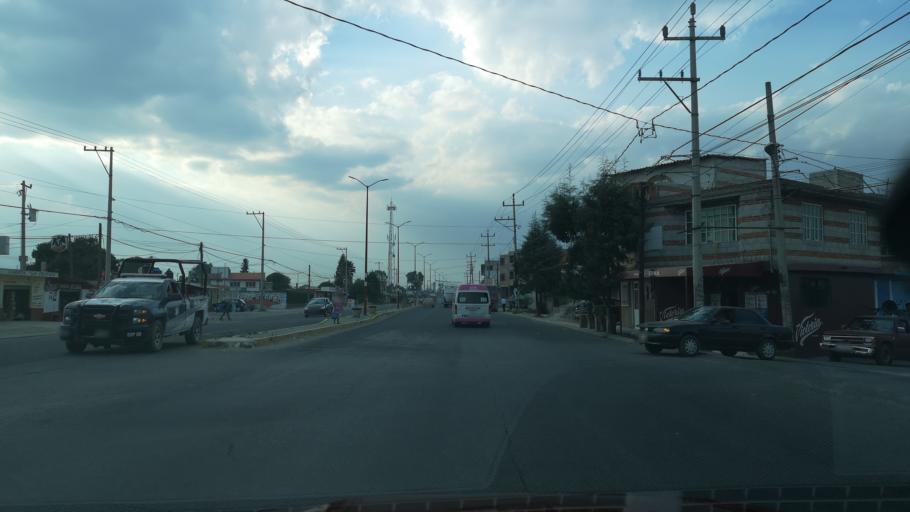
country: MX
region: Puebla
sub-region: Juan C. Bonilla
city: Santa Maria Zacatepec
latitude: 19.1182
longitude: -98.3610
